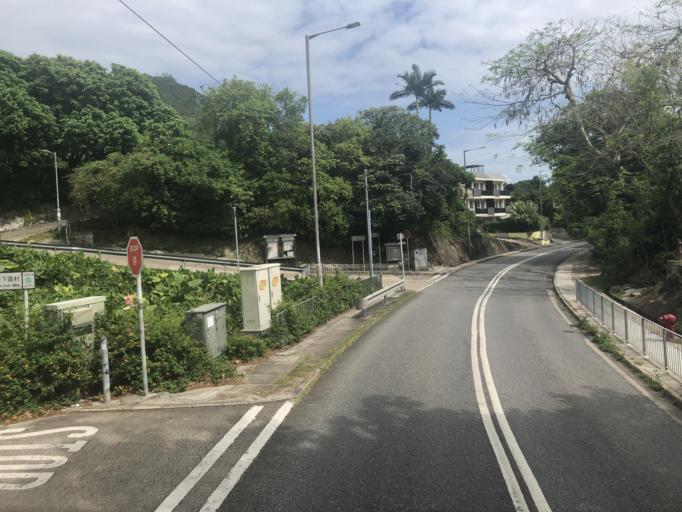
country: HK
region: Sai Kung
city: Sai Kung
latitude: 22.3920
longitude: 114.3001
